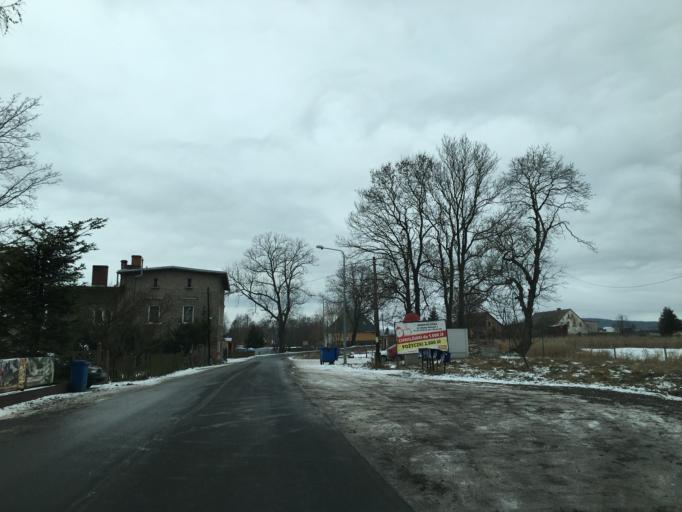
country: PL
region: Lower Silesian Voivodeship
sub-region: Powiat kamiennogorski
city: Krzeszow
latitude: 50.7032
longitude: 16.1195
